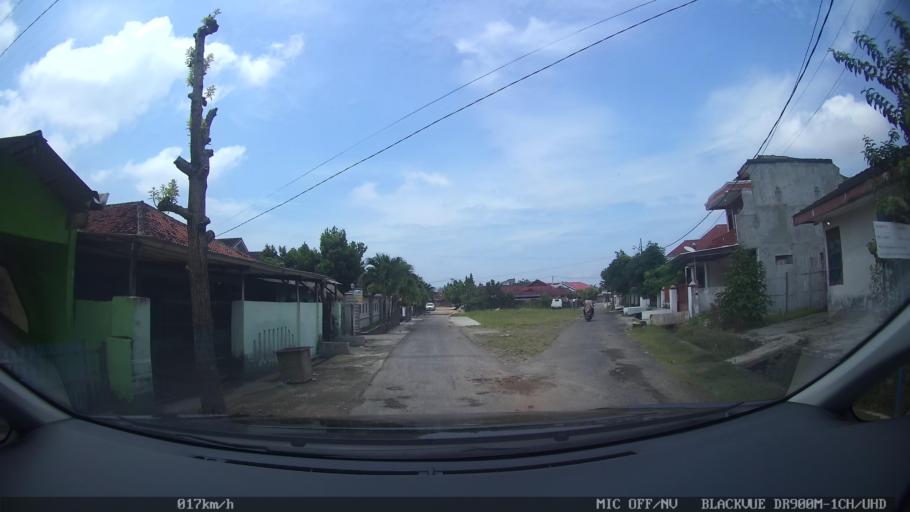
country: ID
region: Lampung
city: Kedaton
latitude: -5.3679
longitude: 105.3040
